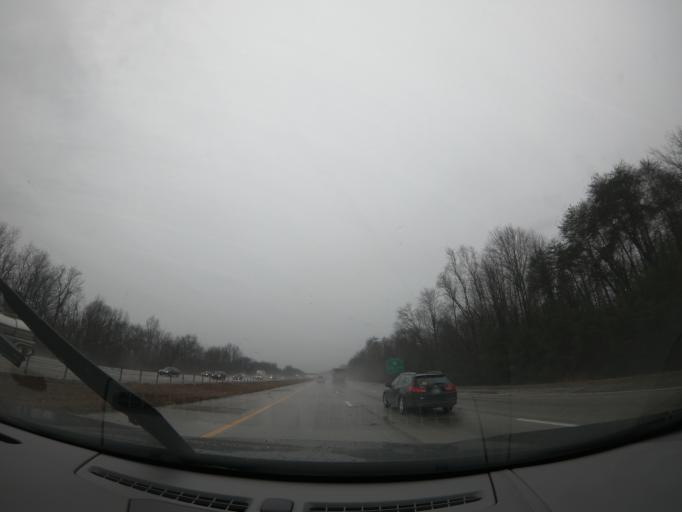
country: US
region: Kentucky
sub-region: Bullitt County
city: Hillview
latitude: 38.0960
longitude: -85.7010
